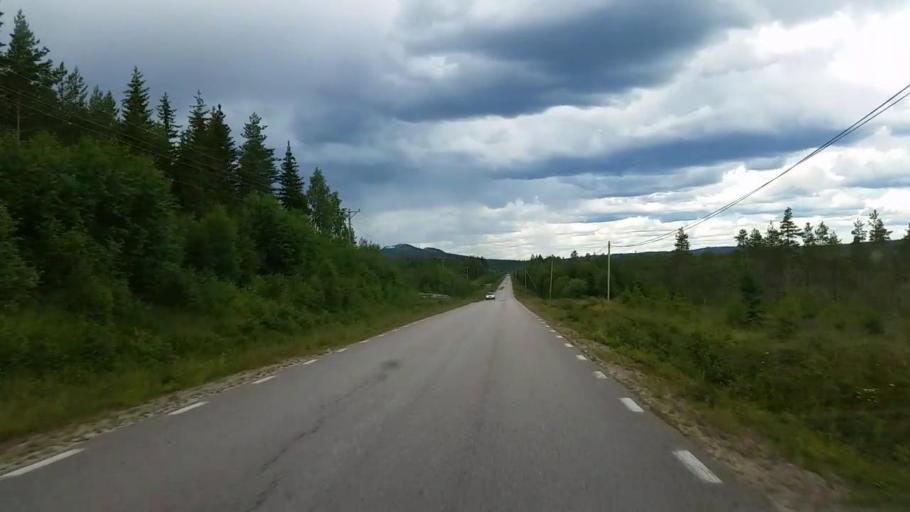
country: SE
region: Gaevleborg
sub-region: Ovanakers Kommun
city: Edsbyn
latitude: 61.4389
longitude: 15.8923
